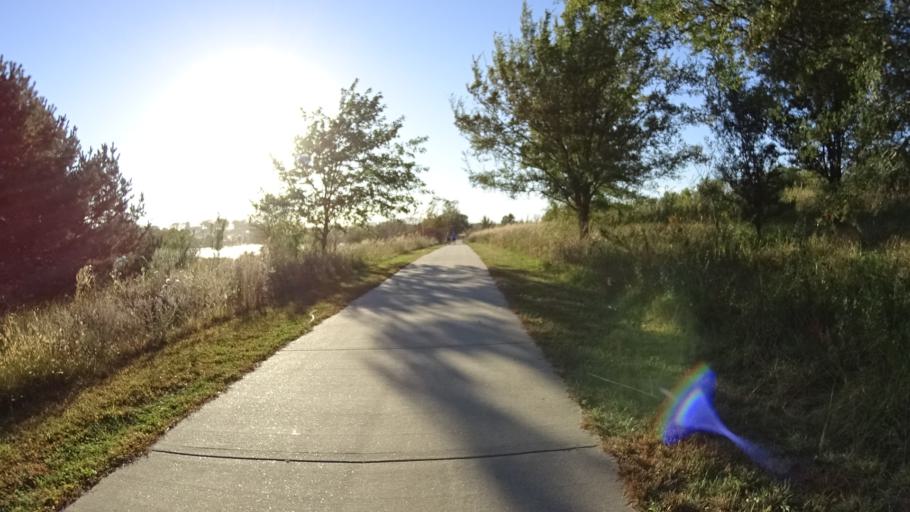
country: US
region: Nebraska
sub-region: Sarpy County
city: Papillion
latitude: 41.1366
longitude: -96.0685
